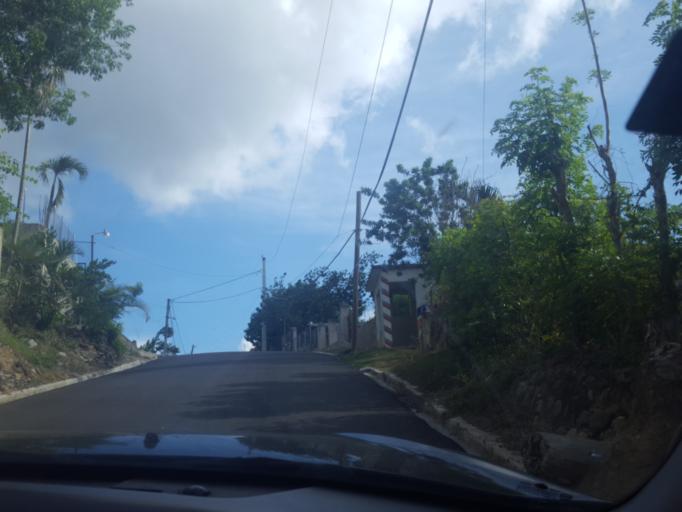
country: DO
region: Santiago
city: Licey al Medio
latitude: 19.3694
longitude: -70.6311
